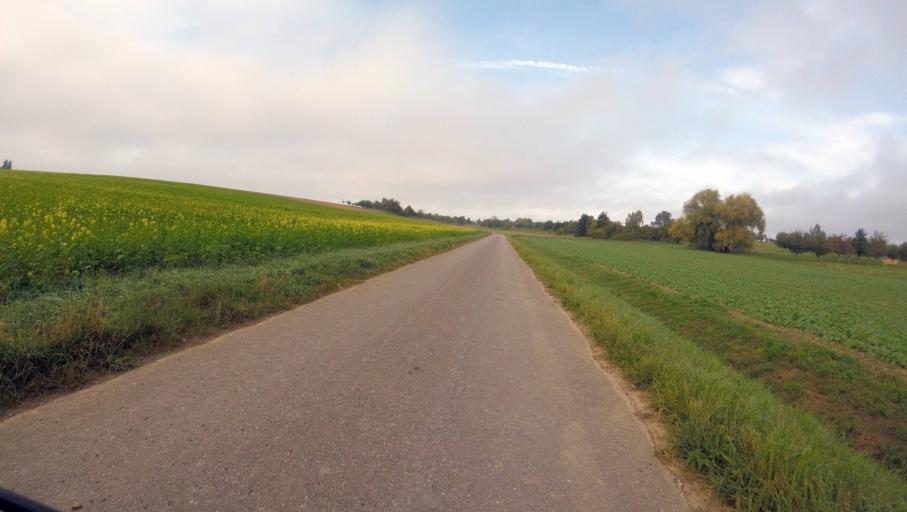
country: DE
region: Baden-Wuerttemberg
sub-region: Regierungsbezirk Stuttgart
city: Motzingen
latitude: 48.5344
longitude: 8.7918
